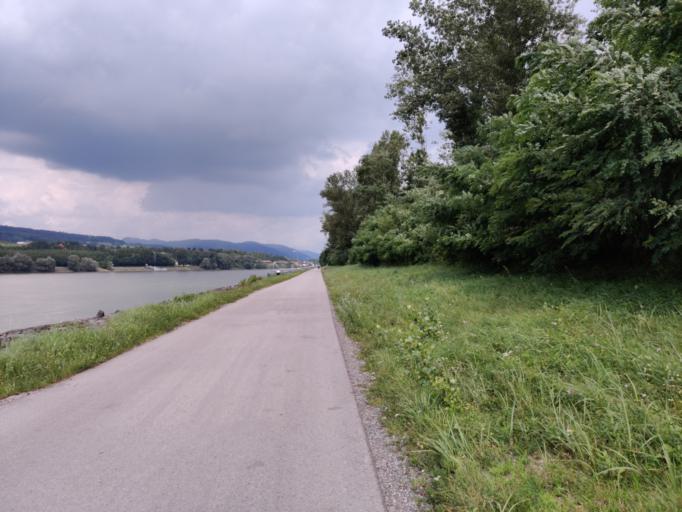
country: AT
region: Lower Austria
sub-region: Politischer Bezirk Melk
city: Melk
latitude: 48.2289
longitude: 15.3209
